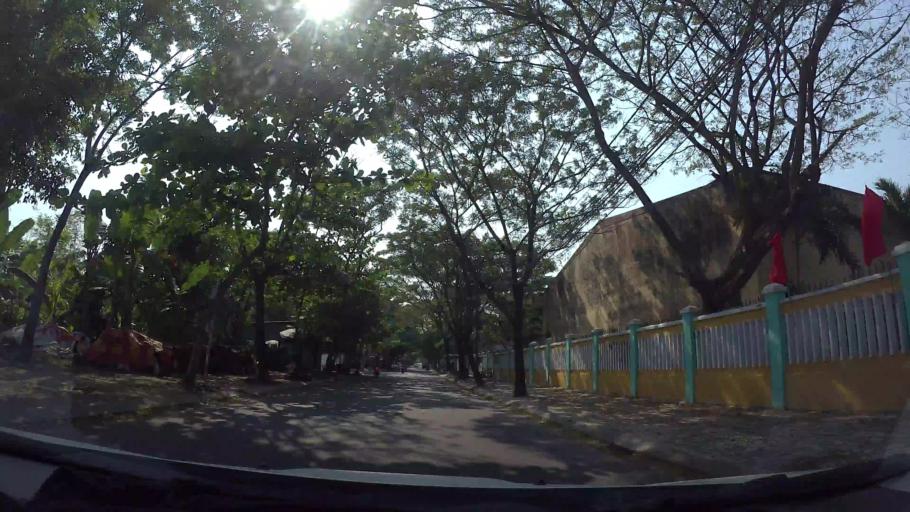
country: VN
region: Da Nang
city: Cam Le
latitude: 16.0061
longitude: 108.1938
